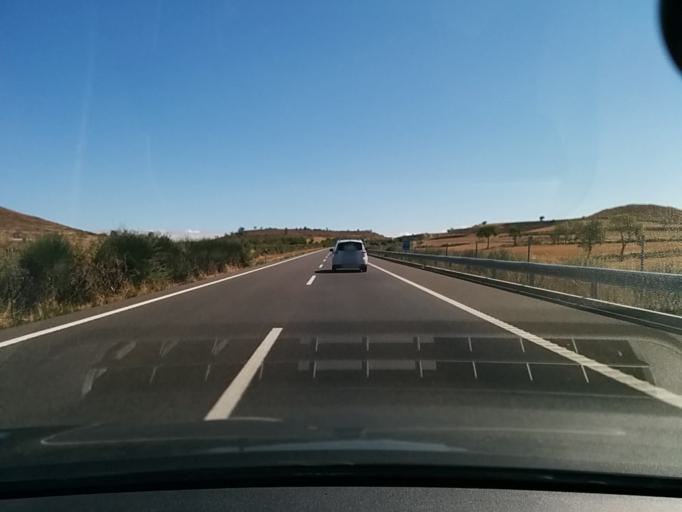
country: ES
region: Aragon
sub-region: Provincia de Huesca
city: Almudebar
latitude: 42.0547
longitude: -0.5449
